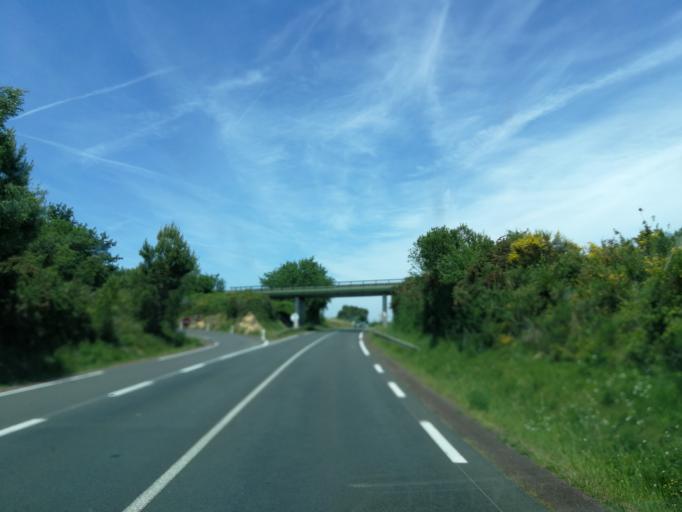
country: FR
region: Pays de la Loire
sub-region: Departement de la Vendee
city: Pissotte
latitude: 46.5476
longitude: -0.8066
